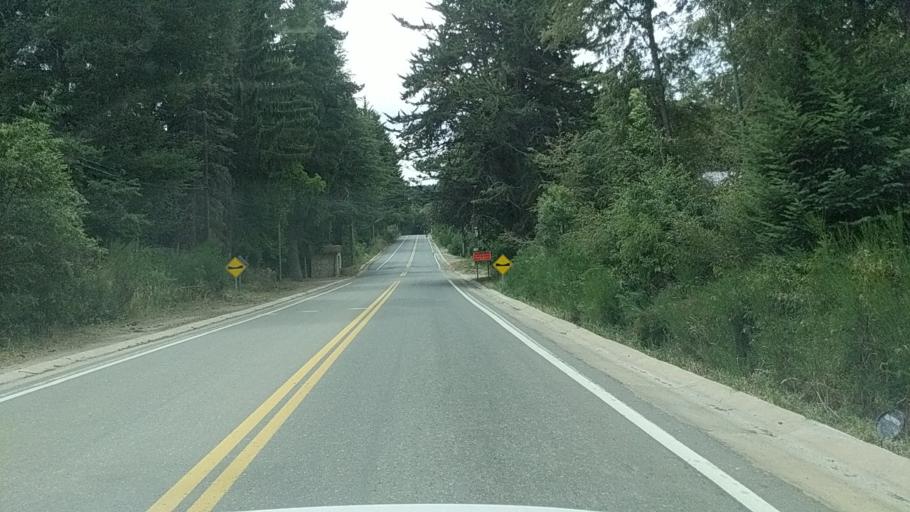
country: AR
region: Neuquen
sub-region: Departamento de Lacar
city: San Martin de los Andes
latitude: -40.1298
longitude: -71.3226
